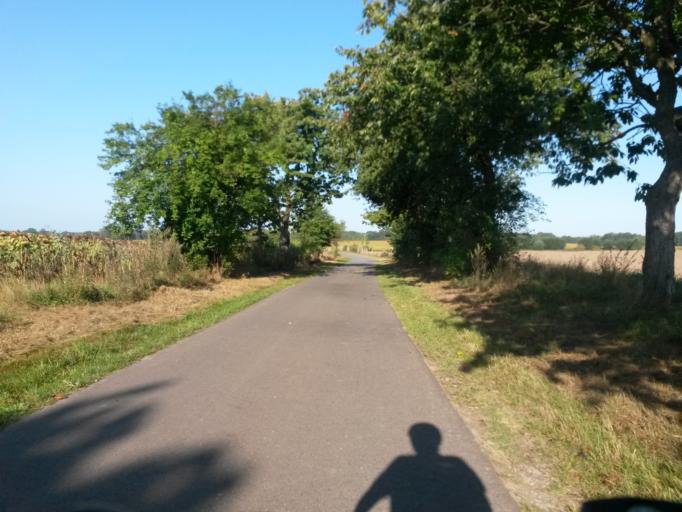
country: DE
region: Brandenburg
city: Templin
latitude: 53.1304
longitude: 13.4645
